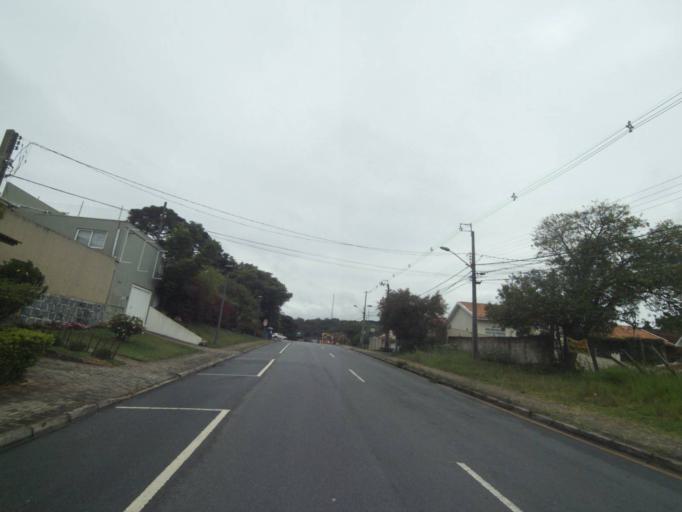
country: BR
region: Parana
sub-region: Curitiba
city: Curitiba
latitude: -25.4134
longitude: -49.2845
